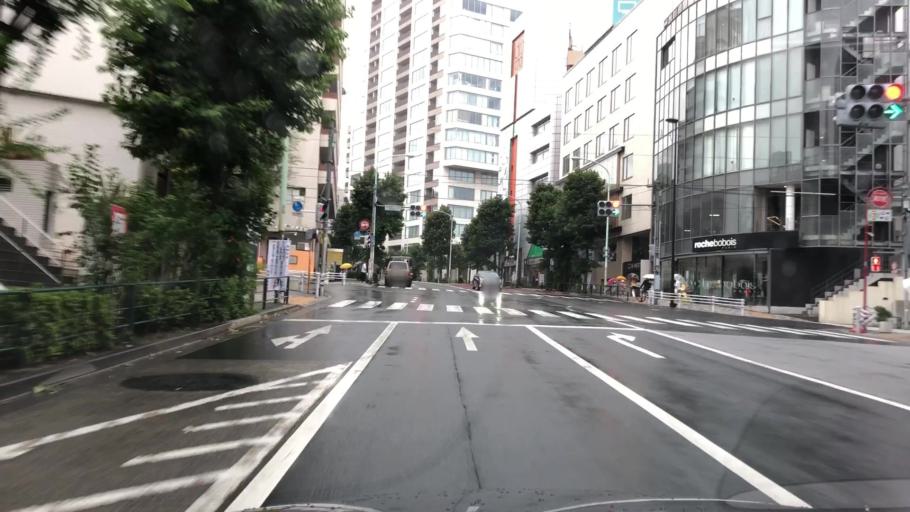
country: JP
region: Tokyo
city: Tokyo
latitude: 35.6727
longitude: 139.7126
